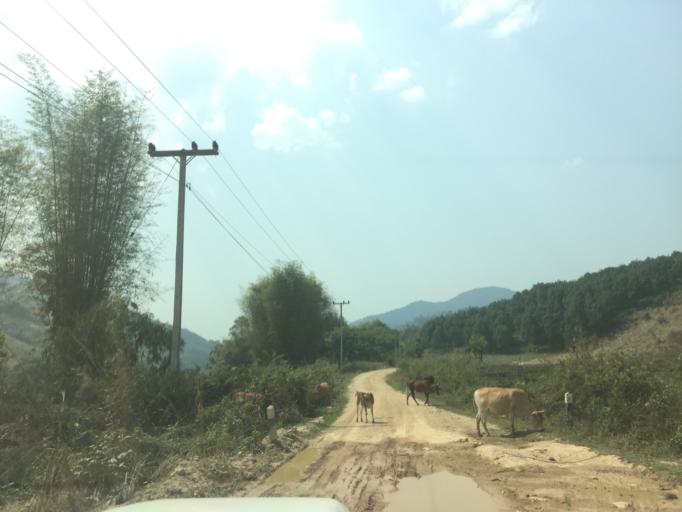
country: TH
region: Nan
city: Song Khwae
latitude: 19.7354
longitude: 100.7242
